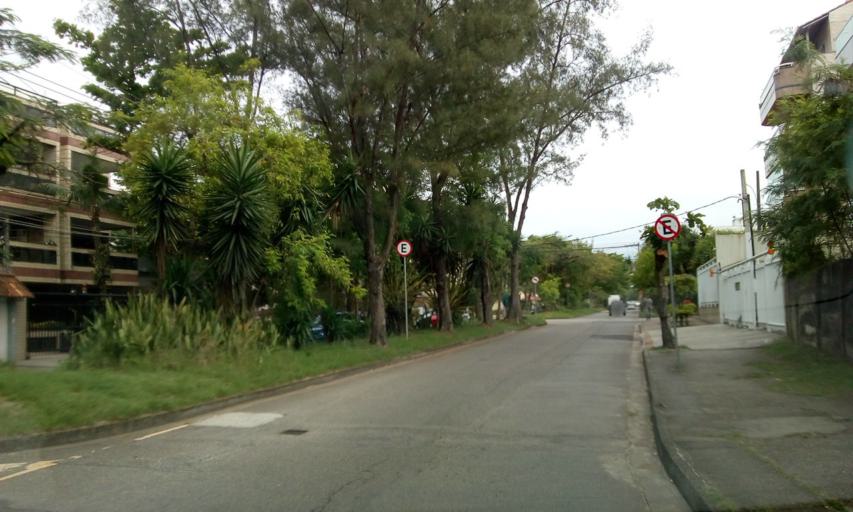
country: BR
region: Rio de Janeiro
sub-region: Nilopolis
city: Nilopolis
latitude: -23.0154
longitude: -43.4551
